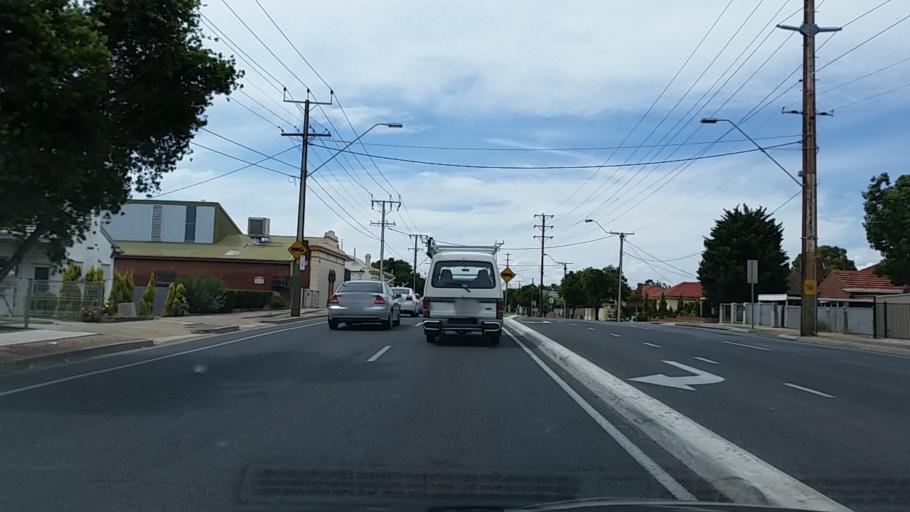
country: AU
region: South Australia
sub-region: City of West Torrens
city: Plympton
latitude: -34.9361
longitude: 138.5527
